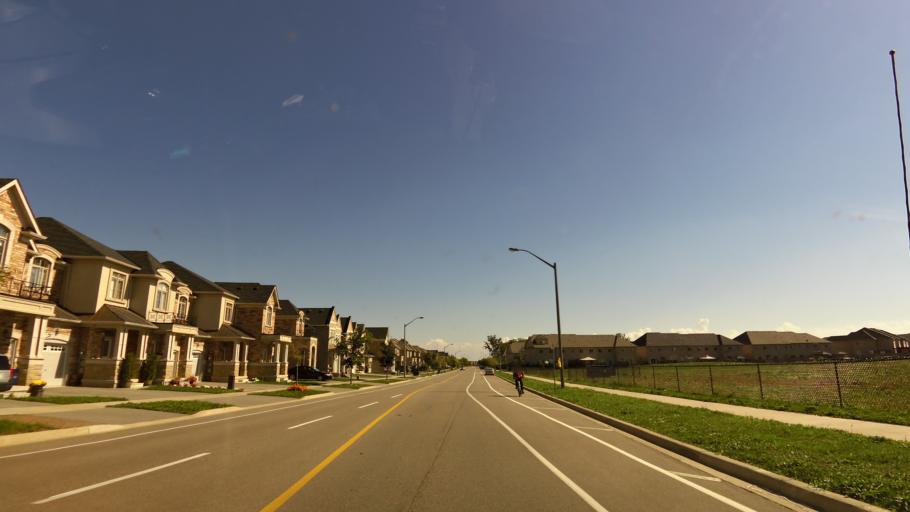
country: CA
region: Ontario
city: Burlington
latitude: 43.4355
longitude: -79.7697
